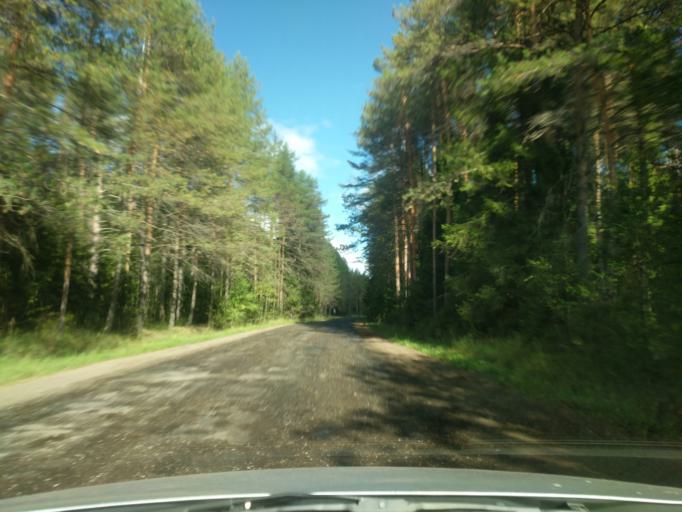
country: RU
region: Kirov
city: Kirovo-Chepetsk
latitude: 58.6042
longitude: 49.9139
